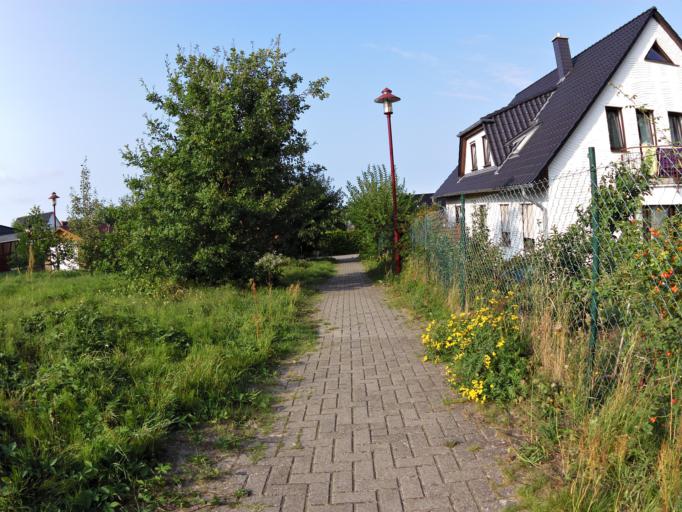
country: DE
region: Mecklenburg-Vorpommern
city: Seebad Bansin
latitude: 53.9569
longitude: 14.1484
